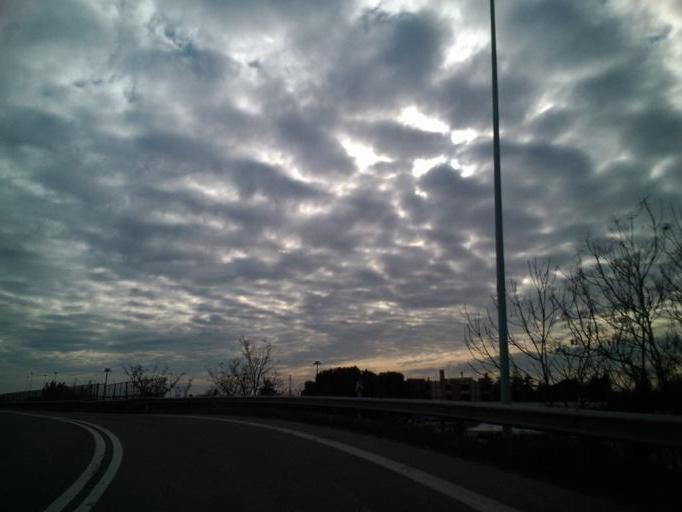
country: IT
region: Veneto
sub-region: Provincia di Verona
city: Monticelli-Fontana
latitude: 45.4215
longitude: 11.1191
